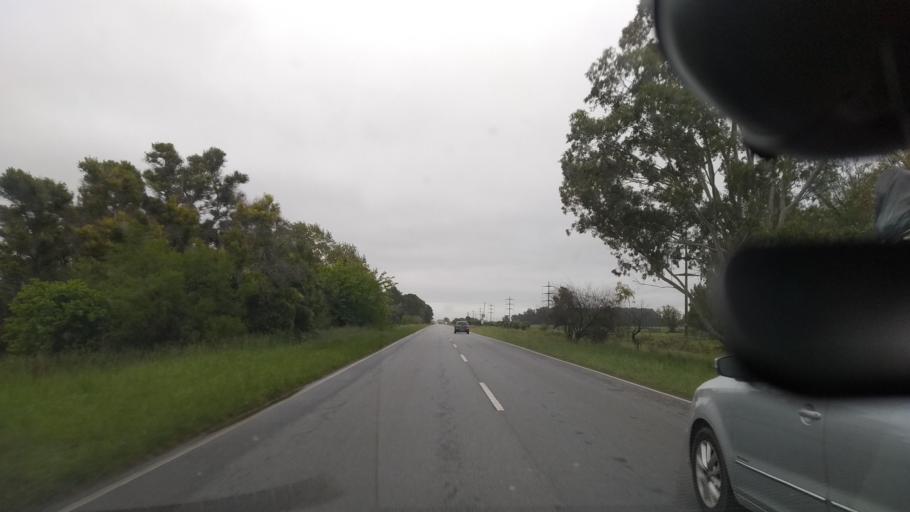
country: AR
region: Buenos Aires
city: Veronica
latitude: -35.3756
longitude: -57.3755
